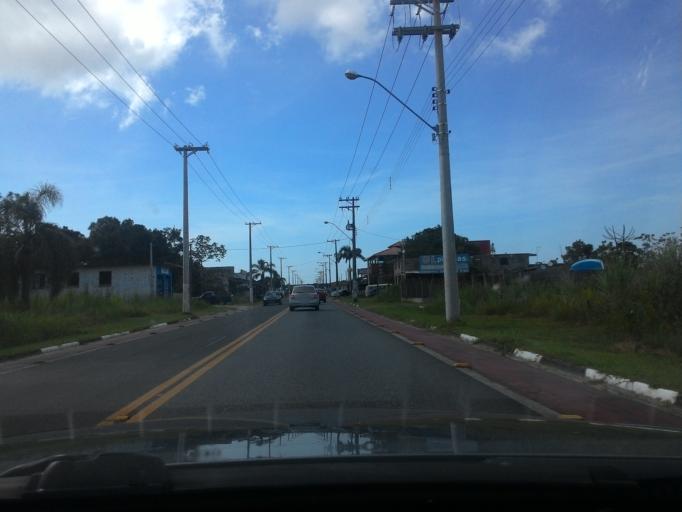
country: BR
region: Sao Paulo
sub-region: Iguape
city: Iguape
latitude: -24.7226
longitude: -47.5340
